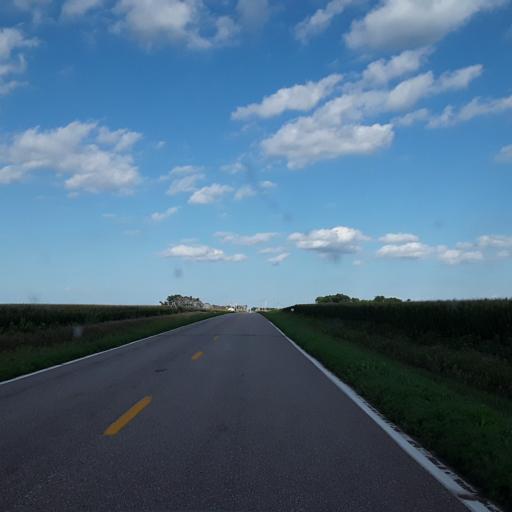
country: US
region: Nebraska
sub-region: Hall County
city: Wood River
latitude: 40.8877
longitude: -98.6148
